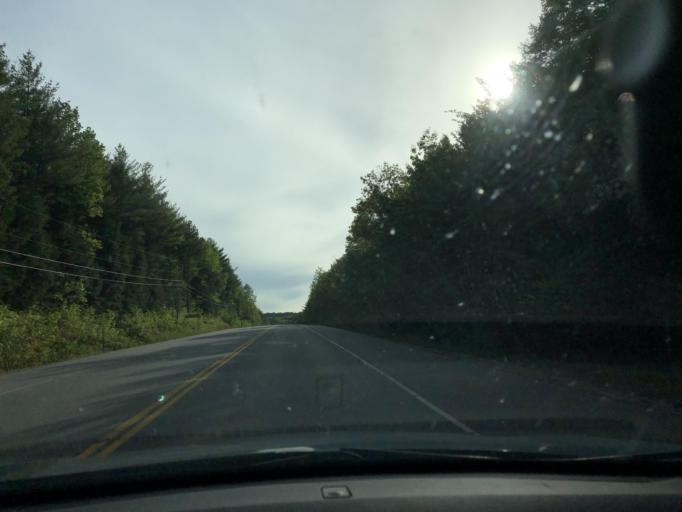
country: US
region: New Hampshire
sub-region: Merrimack County
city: Wilmot
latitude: 43.4170
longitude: -71.9344
